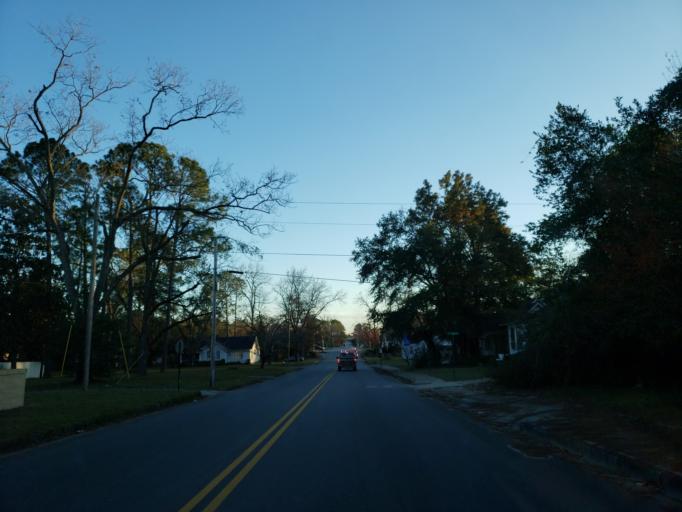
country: US
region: Georgia
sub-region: Crisp County
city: Cordele
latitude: 31.9656
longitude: -83.7795
